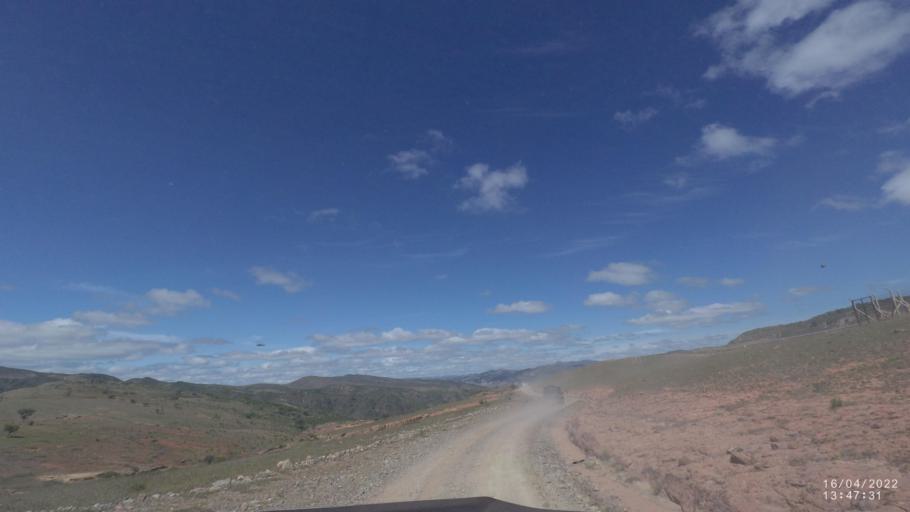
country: BO
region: Cochabamba
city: Mizque
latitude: -18.0087
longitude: -65.5828
